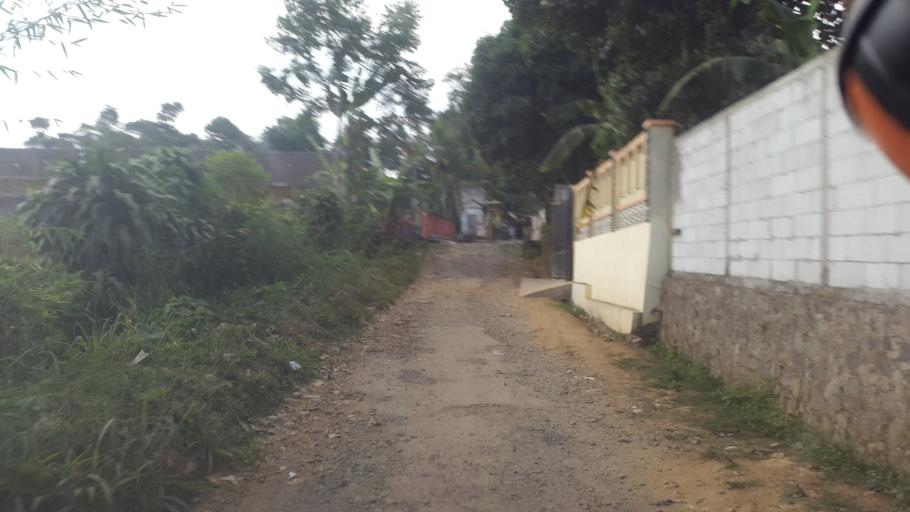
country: ID
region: West Java
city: Sukabumi
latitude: -6.8825
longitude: 106.9588
